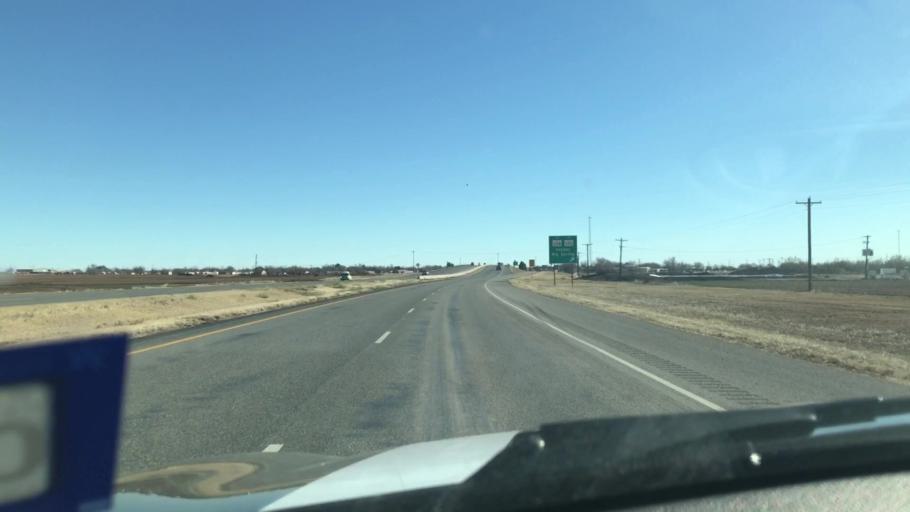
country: US
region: Texas
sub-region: Scurry County
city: Snyder
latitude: 32.7546
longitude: -100.9282
